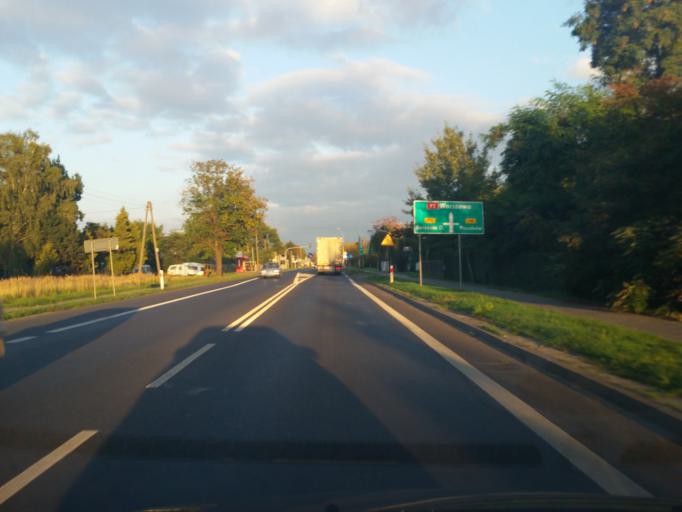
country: PL
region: Masovian Voivodeship
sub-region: Powiat warszawski zachodni
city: Ozarow Mazowiecki
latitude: 52.2112
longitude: 20.7671
